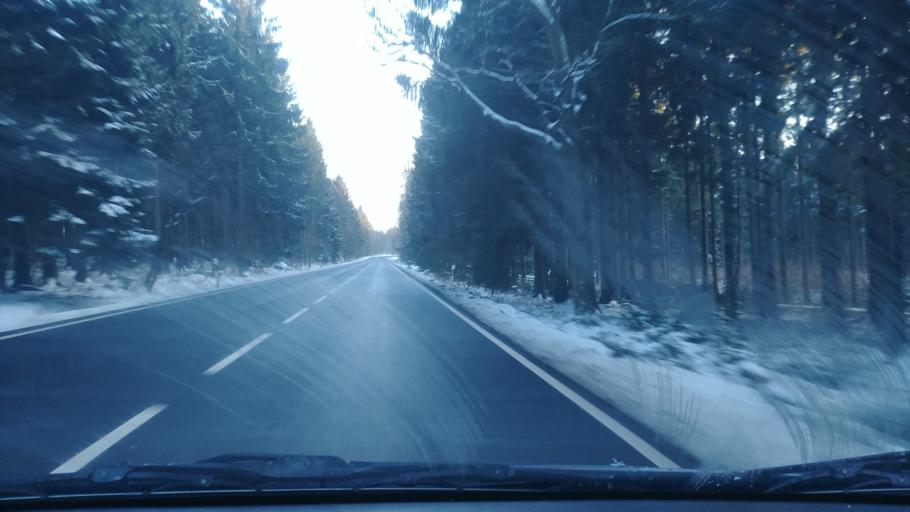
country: DE
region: Lower Saxony
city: Bevern
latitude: 51.7717
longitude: 9.5278
